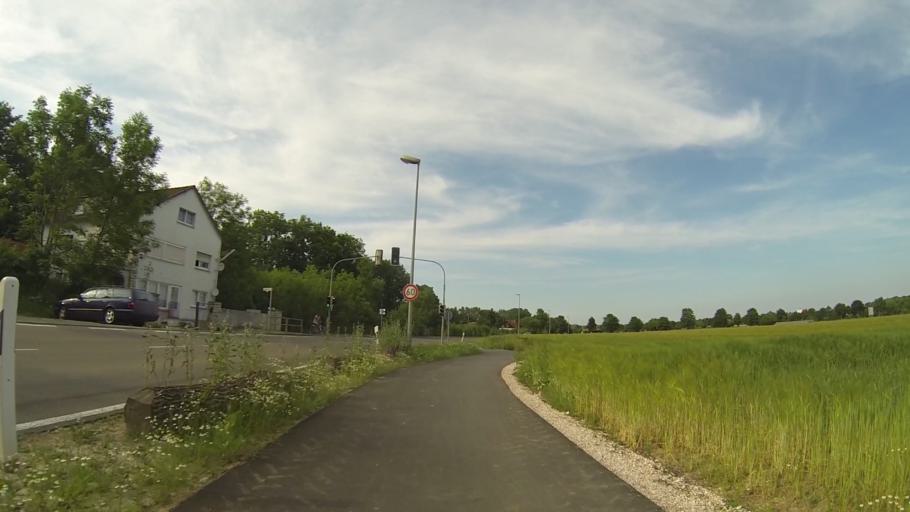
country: DE
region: Baden-Wuerttemberg
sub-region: Tuebingen Region
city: Ulm
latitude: 48.3571
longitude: 9.9602
